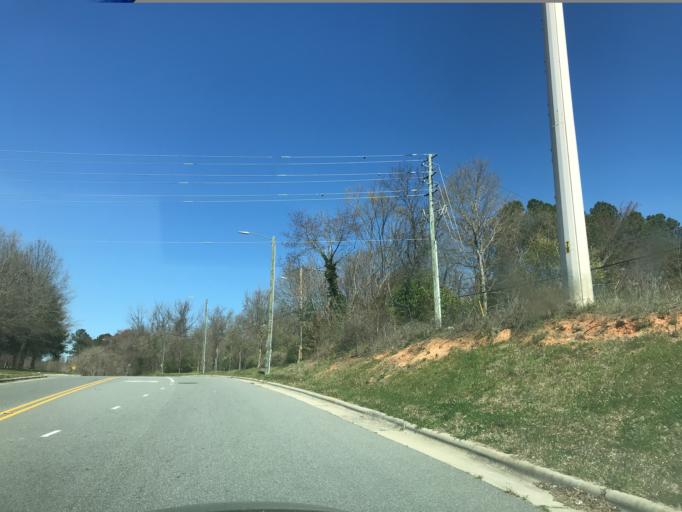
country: US
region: North Carolina
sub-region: Wake County
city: Raleigh
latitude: 35.7583
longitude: -78.6413
